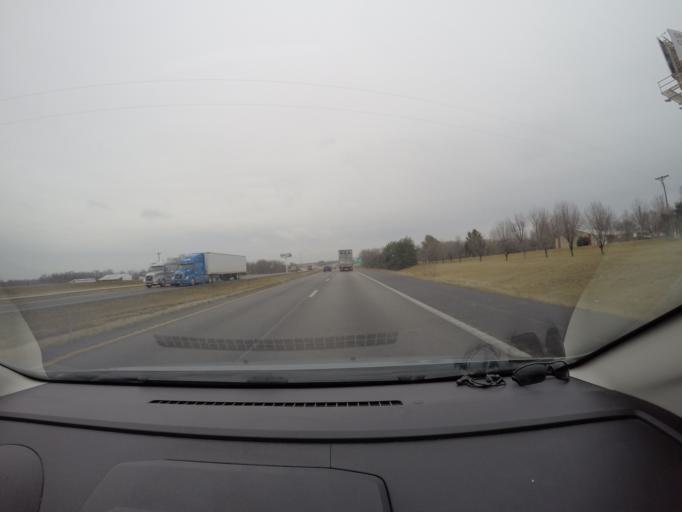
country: US
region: Missouri
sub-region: Warren County
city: Warrenton
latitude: 38.8603
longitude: -91.3117
